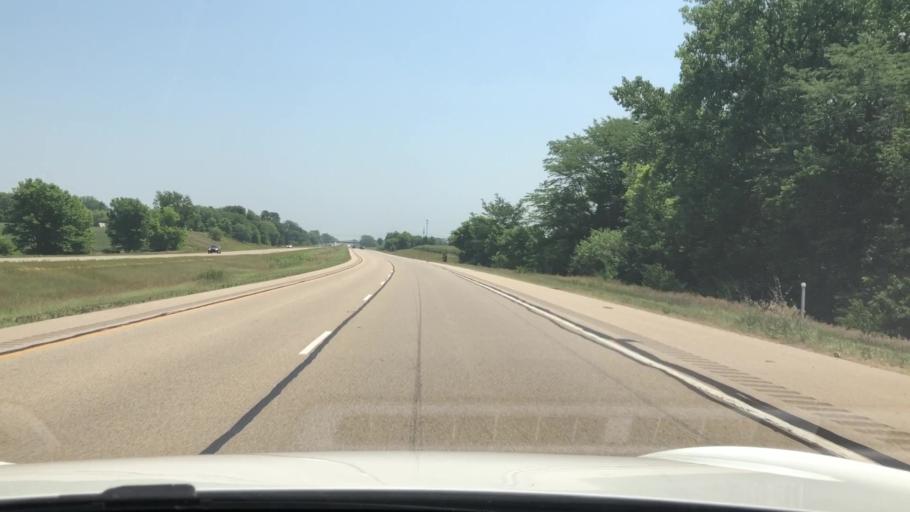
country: US
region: Illinois
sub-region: McLean County
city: Bloomington
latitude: 40.4216
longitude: -88.9476
